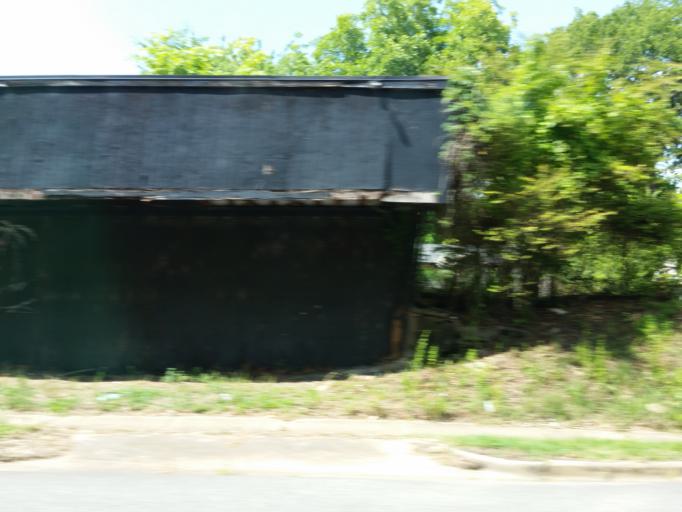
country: US
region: Alabama
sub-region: Greene County
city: Eutaw
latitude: 32.8406
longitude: -87.8840
